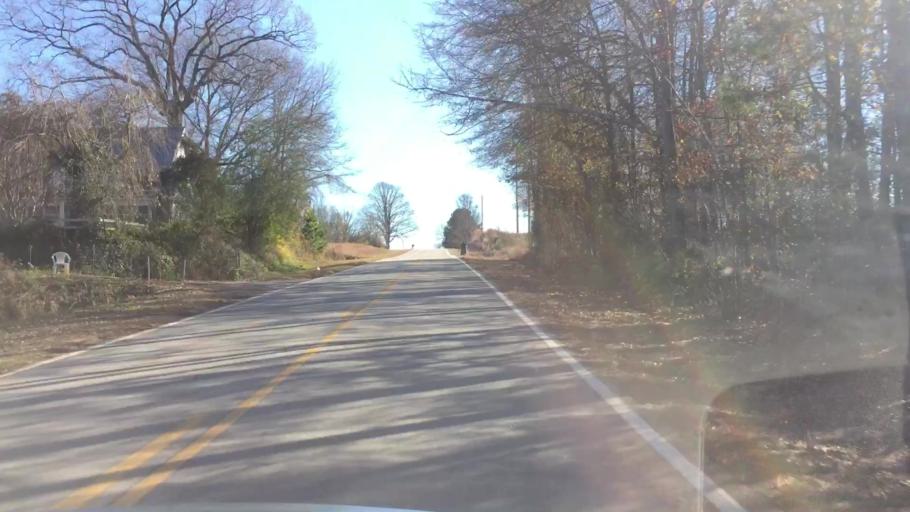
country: US
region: Georgia
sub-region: Newton County
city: Oakwood
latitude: 33.4989
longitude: -84.0486
